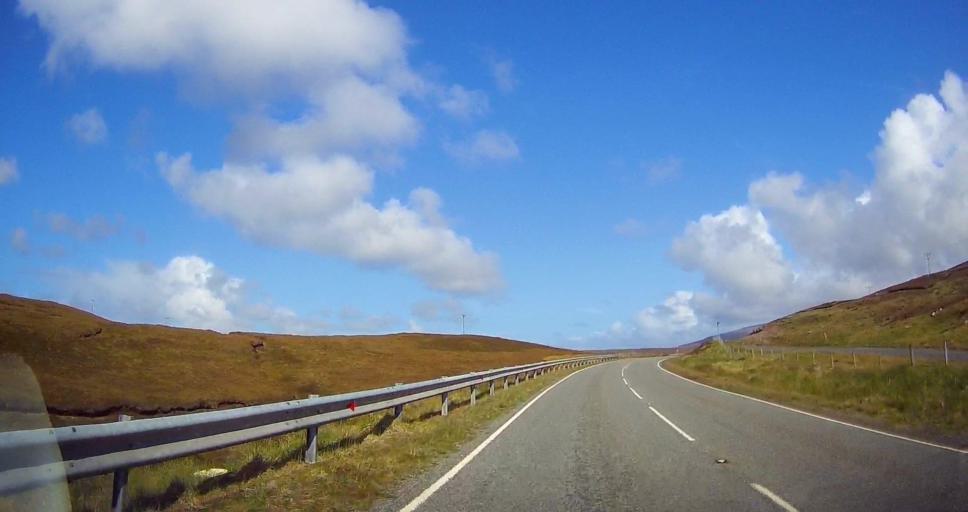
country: GB
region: Scotland
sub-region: Shetland Islands
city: Lerwick
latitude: 60.4591
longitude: -1.4013
